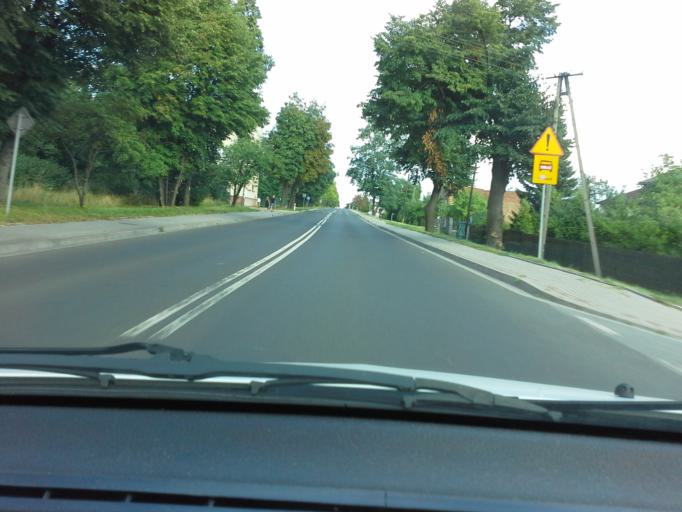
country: PL
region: Lesser Poland Voivodeship
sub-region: Powiat chrzanowski
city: Trzebinia
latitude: 50.1496
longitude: 19.4924
